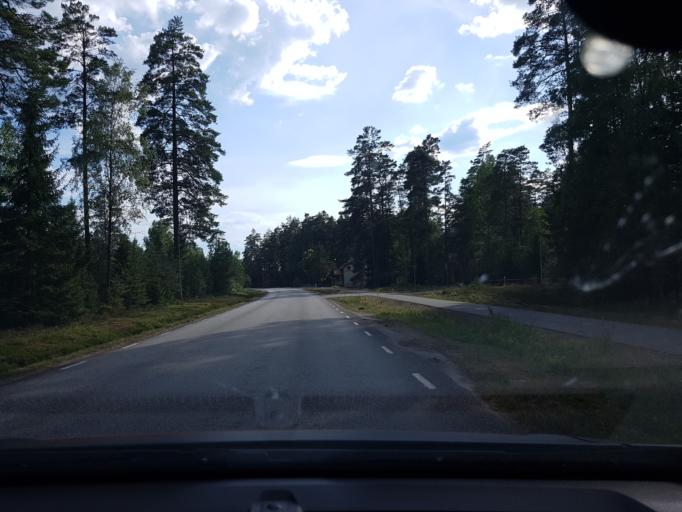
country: SE
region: Joenkoeping
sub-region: Gislaveds Kommun
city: Gislaved
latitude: 57.2854
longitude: 13.5468
